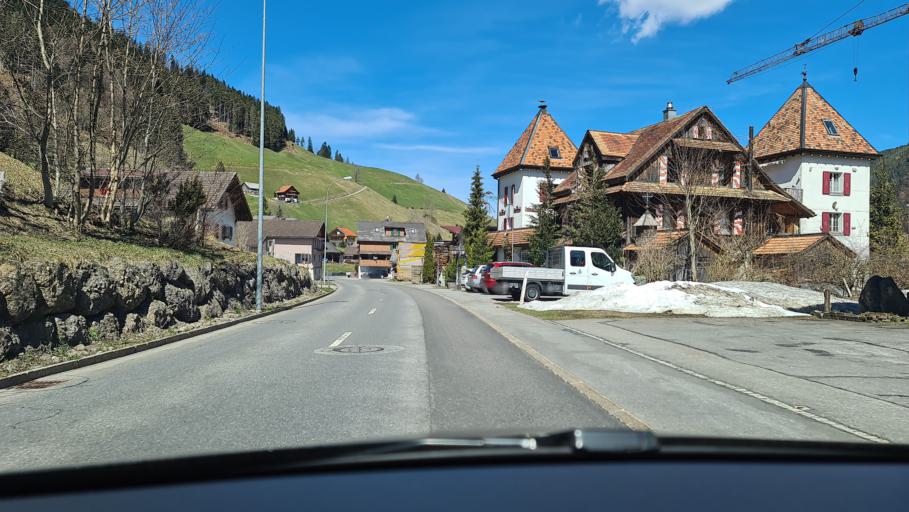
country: CH
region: Schwyz
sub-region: Bezirk Schwyz
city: Rothenthurm
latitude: 47.0670
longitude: 8.7147
